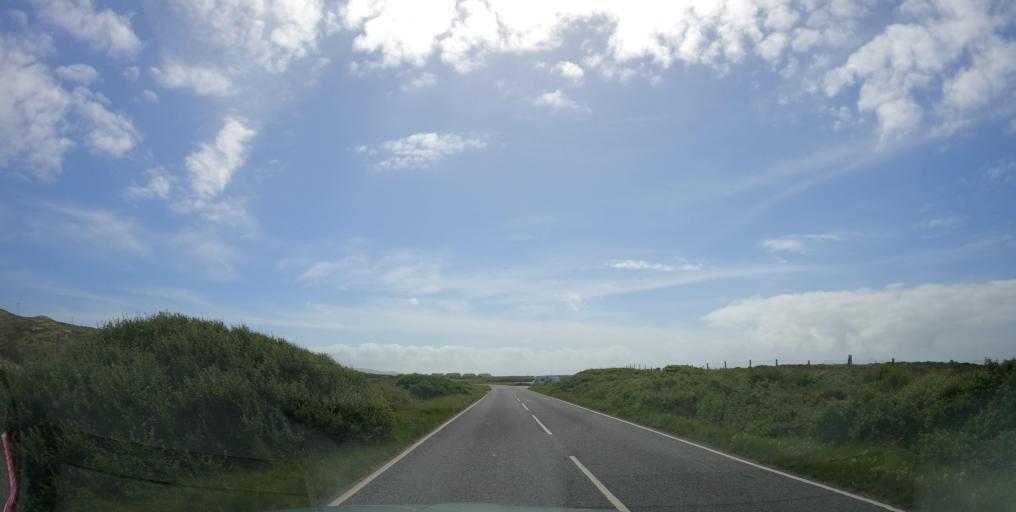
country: GB
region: Scotland
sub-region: Eilean Siar
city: Isle of South Uist
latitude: 57.1912
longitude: -7.3887
